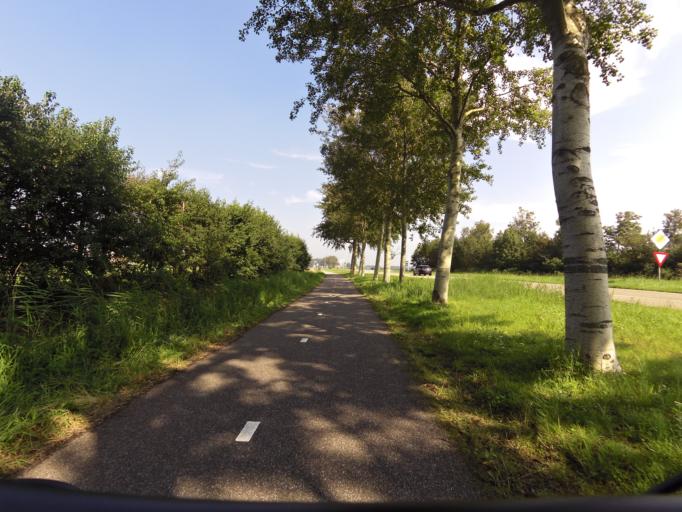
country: NL
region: Zeeland
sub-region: Schouwen-Duiveland
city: Burgh
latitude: 51.6796
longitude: 3.7241
